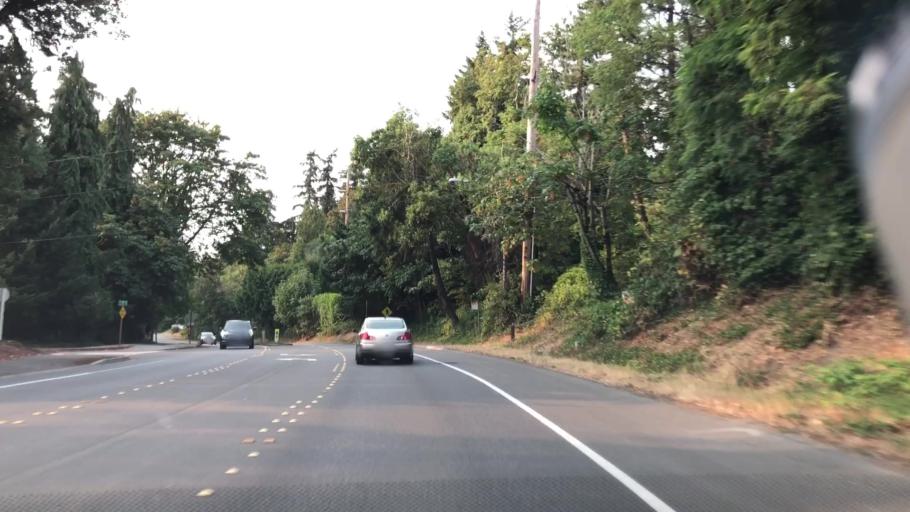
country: US
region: Washington
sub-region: King County
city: Mercer Island
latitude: 47.5597
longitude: -122.2206
